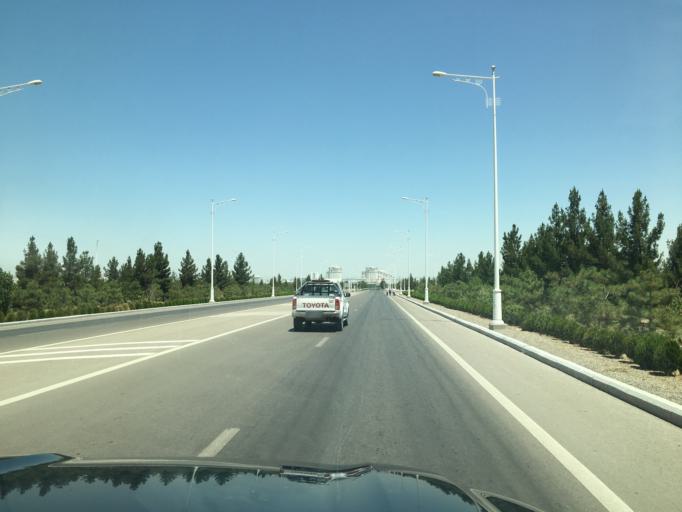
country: TM
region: Ahal
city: Ashgabat
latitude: 37.8621
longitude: 58.3764
